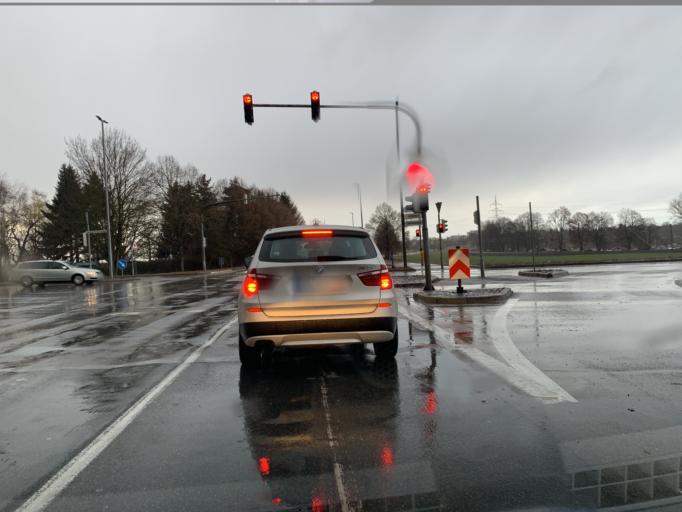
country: DE
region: Baden-Wuerttemberg
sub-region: Regierungsbezirk Stuttgart
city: Magstadt
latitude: 48.7107
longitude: 8.9797
